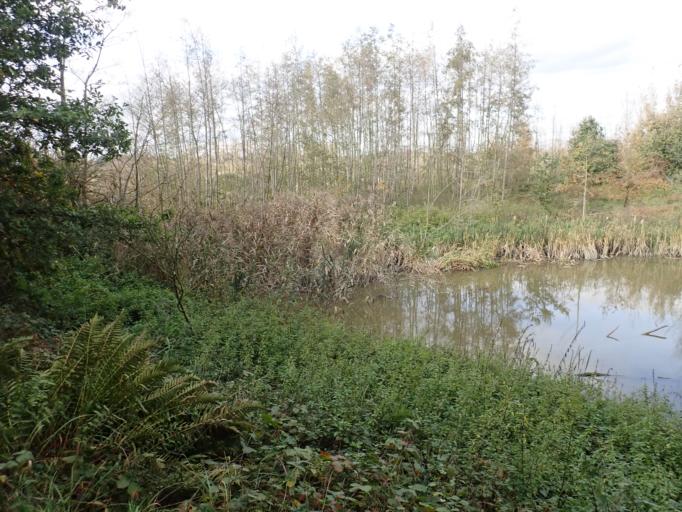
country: BE
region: Flanders
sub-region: Provincie Oost-Vlaanderen
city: Kruibeke
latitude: 51.1578
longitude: 4.3161
